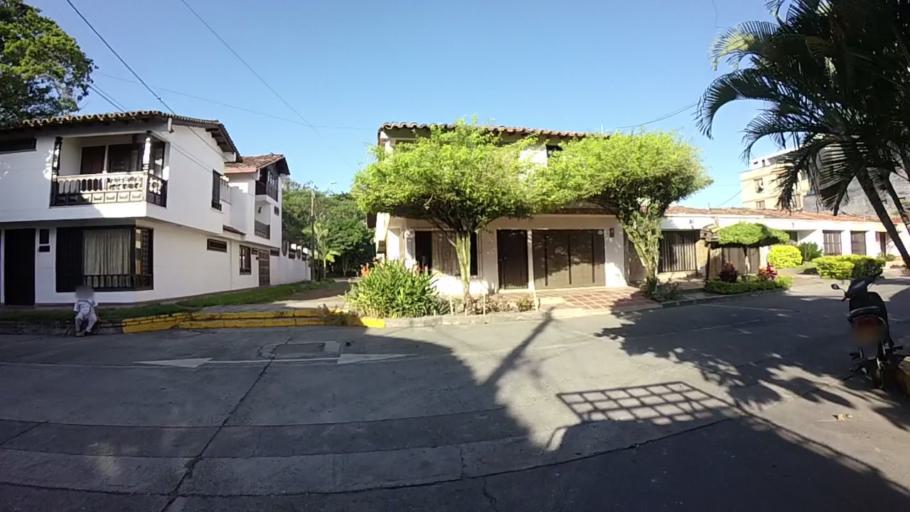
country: CO
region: Valle del Cauca
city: Cartago
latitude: 4.7543
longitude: -75.9151
